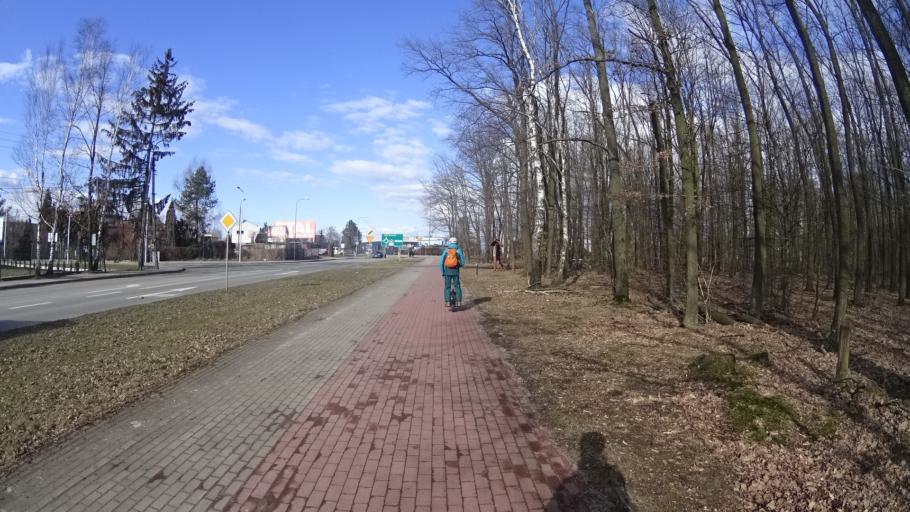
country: PL
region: Masovian Voivodeship
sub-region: Powiat warszawski zachodni
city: Babice
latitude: 52.2746
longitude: 20.8653
